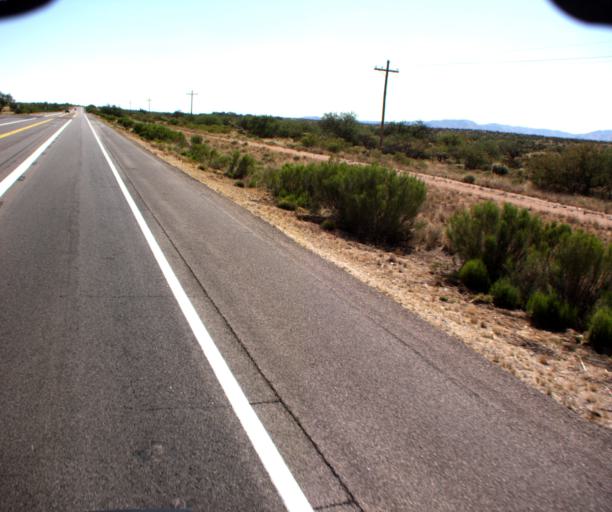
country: US
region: Arizona
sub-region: Pima County
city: Catalina
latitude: 32.5793
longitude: -110.9132
